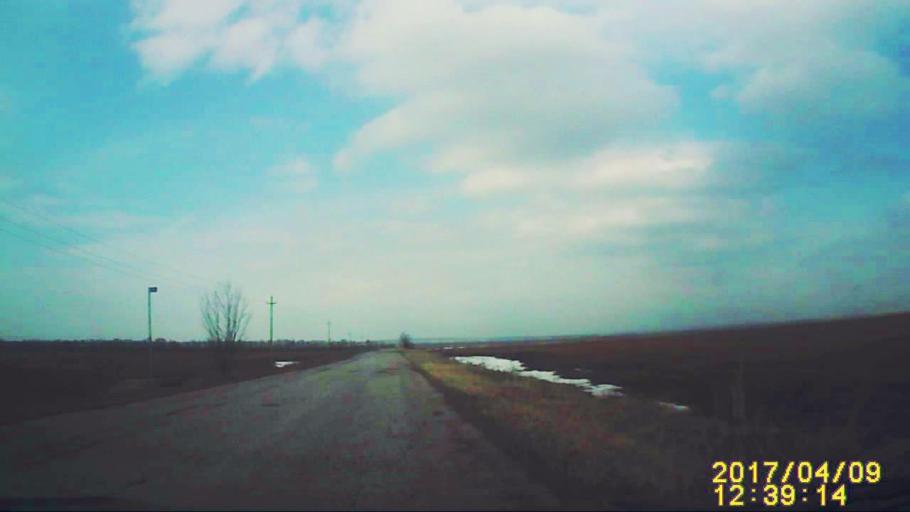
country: RU
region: Ulyanovsk
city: Ignatovka
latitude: 53.9981
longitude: 47.9585
